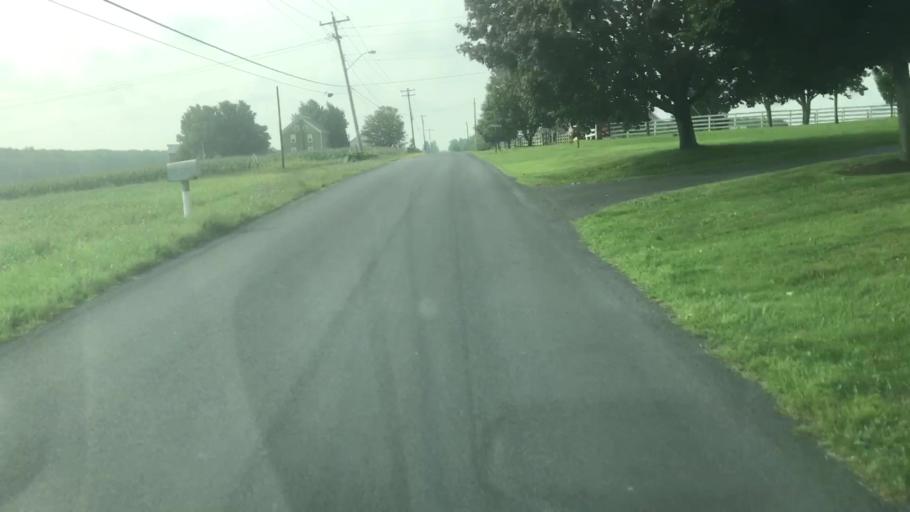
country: US
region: New York
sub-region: Onondaga County
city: Skaneateles
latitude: 42.9291
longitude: -76.4574
